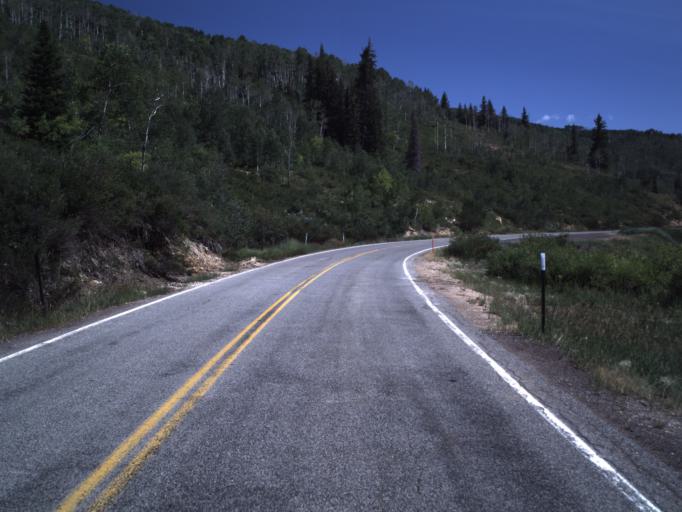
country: US
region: Utah
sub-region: Sanpete County
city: Fairview
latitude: 39.6716
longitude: -111.3396
